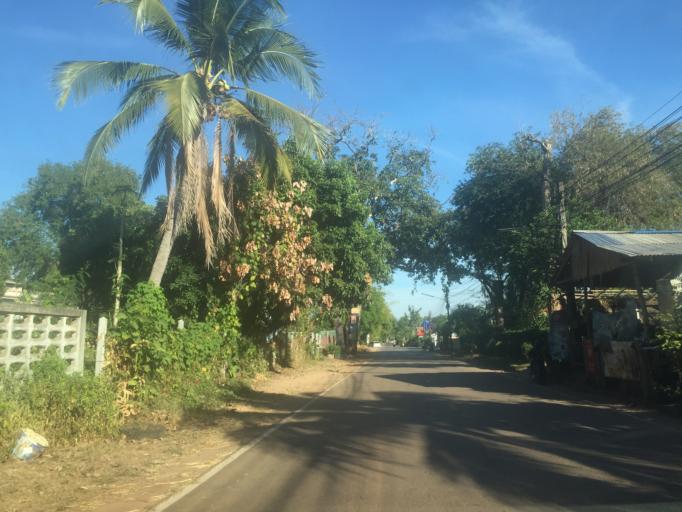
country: TH
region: Changwat Udon Thani
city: Si That
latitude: 16.9720
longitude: 103.2172
